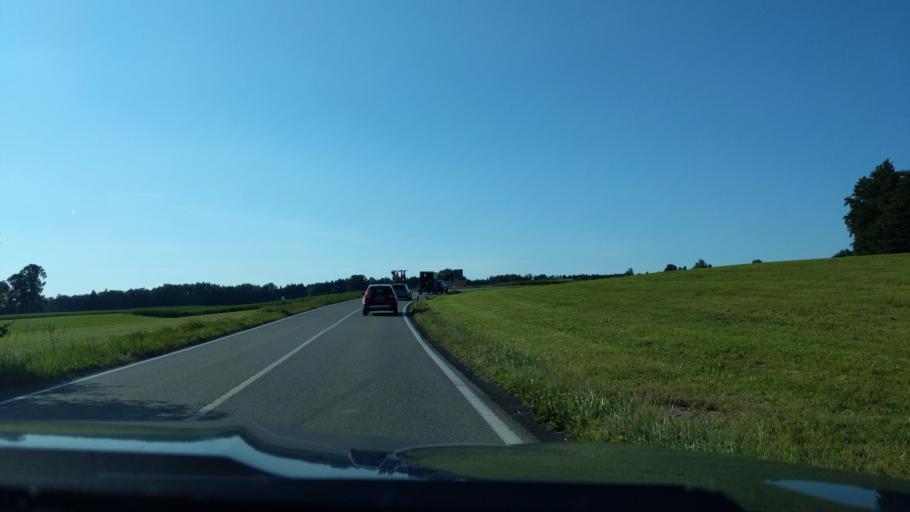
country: DE
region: Bavaria
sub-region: Upper Bavaria
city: Tuntenhausen
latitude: 47.9310
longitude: 11.9822
